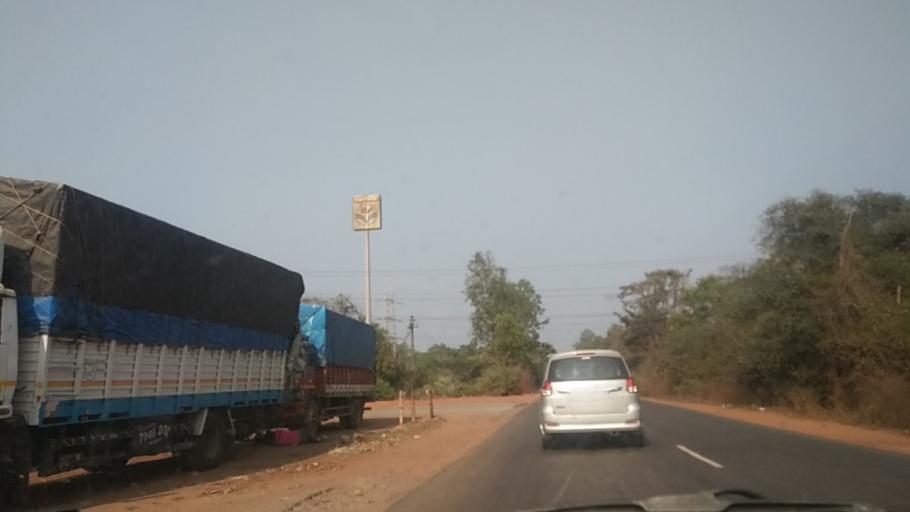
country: IN
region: Goa
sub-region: North Goa
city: Colovale
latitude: 15.6289
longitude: 73.8262
